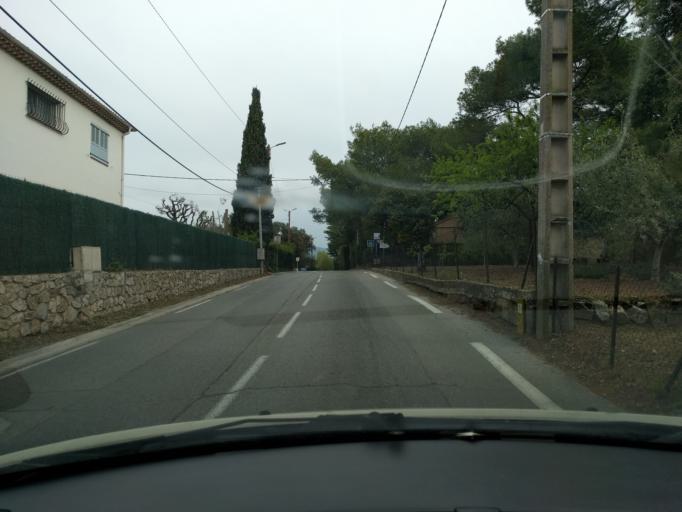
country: FR
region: Provence-Alpes-Cote d'Azur
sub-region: Departement des Alpes-Maritimes
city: La Roquette-sur-Siagne
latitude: 43.5871
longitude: 6.9571
